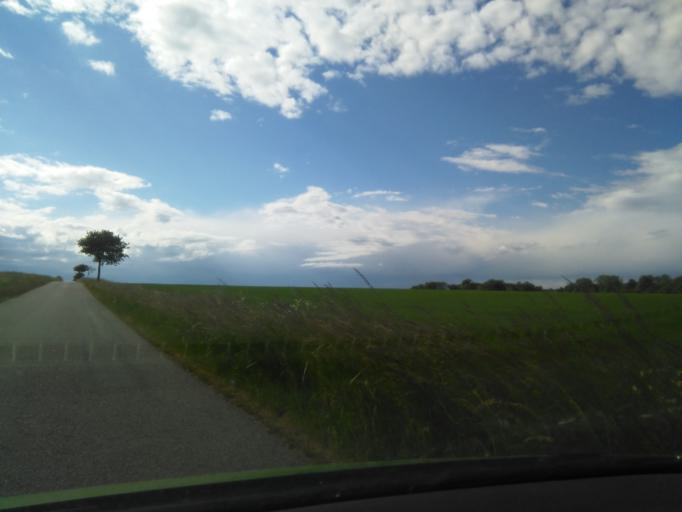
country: DK
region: Capital Region
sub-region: Bornholm Kommune
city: Nexo
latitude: 55.1248
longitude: 15.0630
